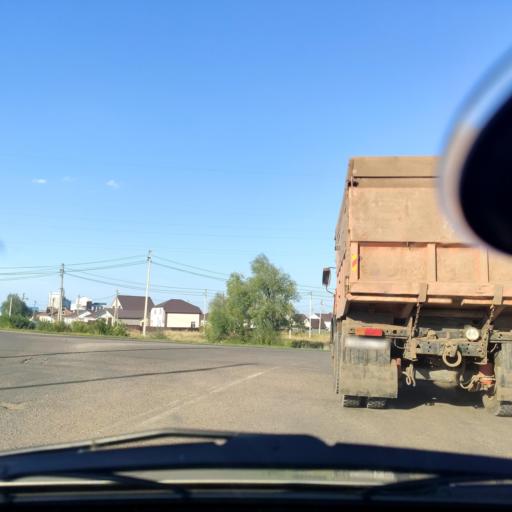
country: RU
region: Bashkortostan
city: Meleuz
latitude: 52.9505
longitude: 55.9051
